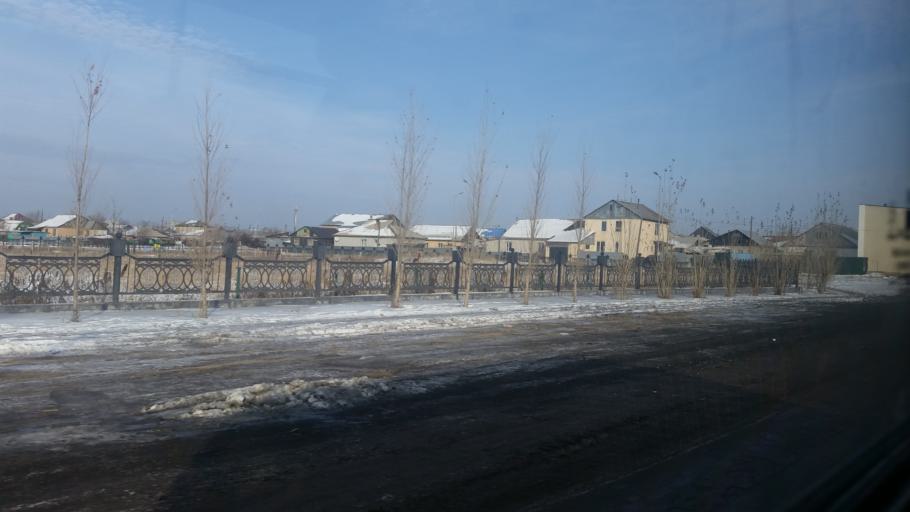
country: KZ
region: Astana Qalasy
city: Astana
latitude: 51.1857
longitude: 71.3955
